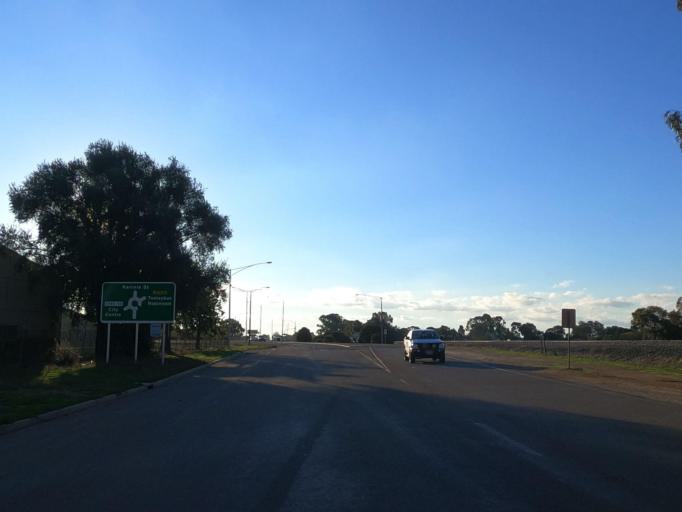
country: AU
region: Victoria
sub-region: Swan Hill
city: Swan Hill
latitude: -35.3284
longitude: 143.5546
